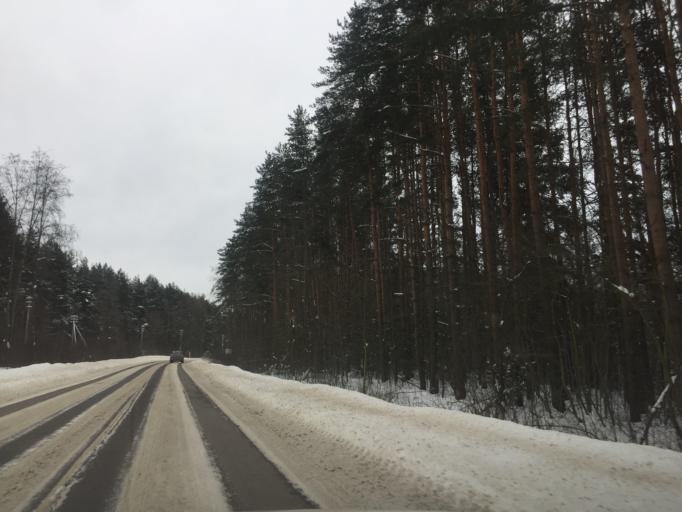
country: RU
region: Leningrad
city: Imeni Sverdlova
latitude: 59.7879
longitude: 30.7231
